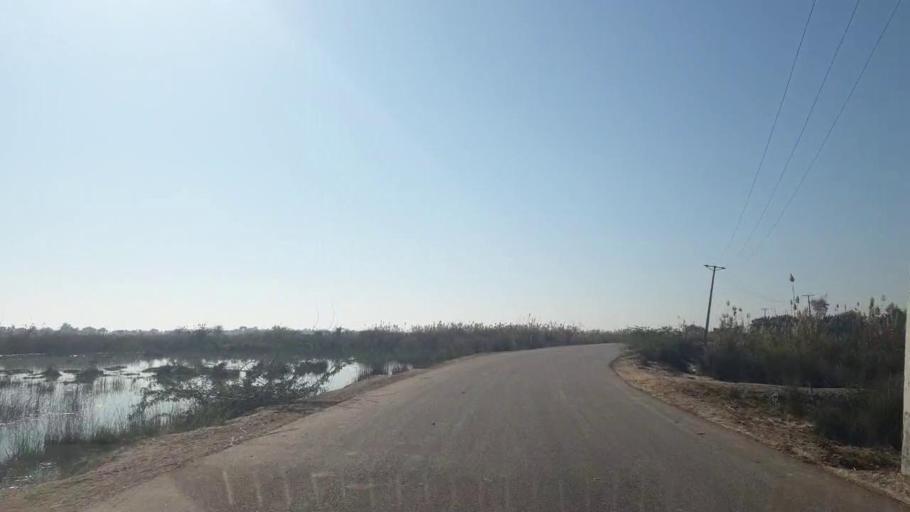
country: PK
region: Sindh
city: Kot Diji
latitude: 27.3143
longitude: 68.6491
